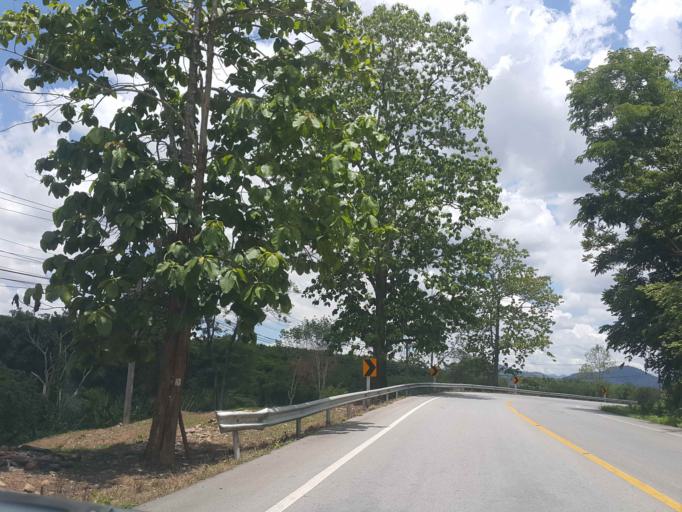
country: TH
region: Nan
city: Wiang Sa
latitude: 18.5252
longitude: 100.6144
